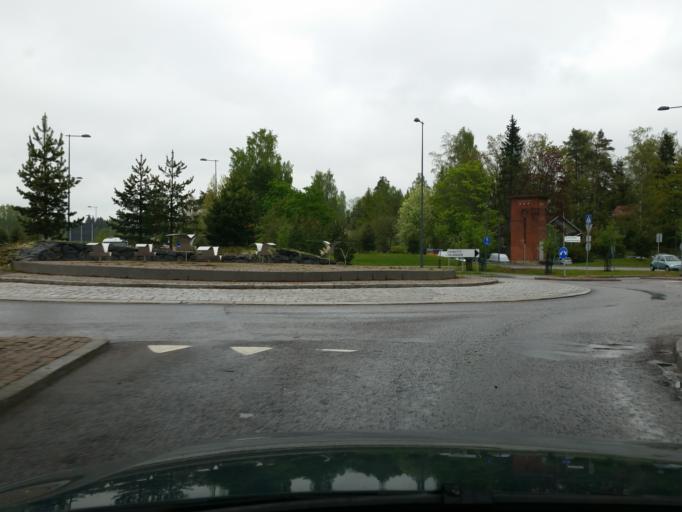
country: FI
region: Uusimaa
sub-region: Helsinki
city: Teekkarikylae
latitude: 60.2296
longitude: 24.8247
